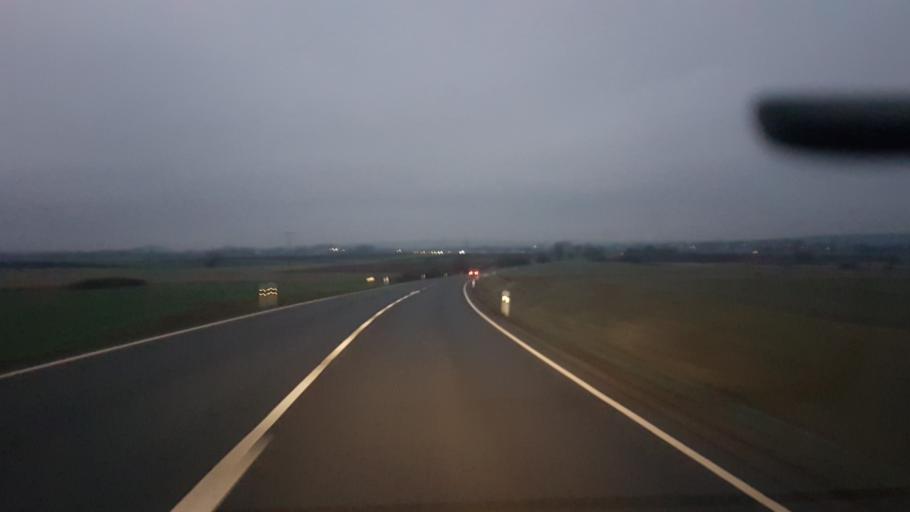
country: DE
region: Bavaria
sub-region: Regierungsbezirk Unterfranken
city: Bad Konigshofen im Grabfeld
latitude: 50.2803
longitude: 10.4936
